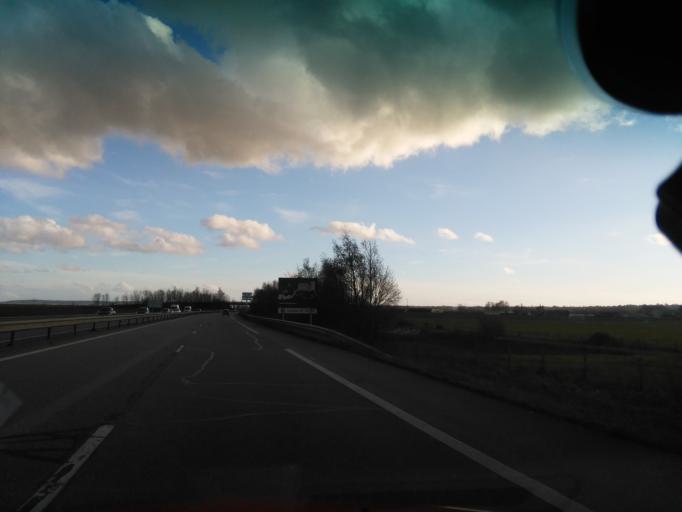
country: FR
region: Lower Normandy
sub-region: Departement du Calvados
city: Falaise
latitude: 48.9251
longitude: -0.2065
